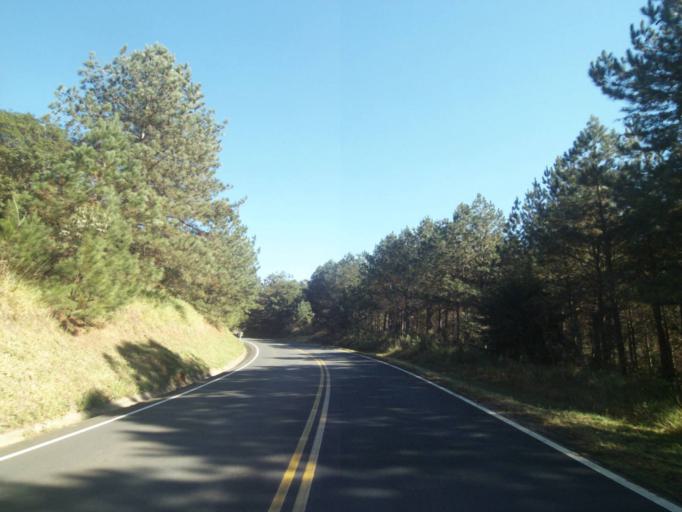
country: BR
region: Parana
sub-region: Tibagi
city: Tibagi
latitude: -24.4694
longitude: -50.5333
